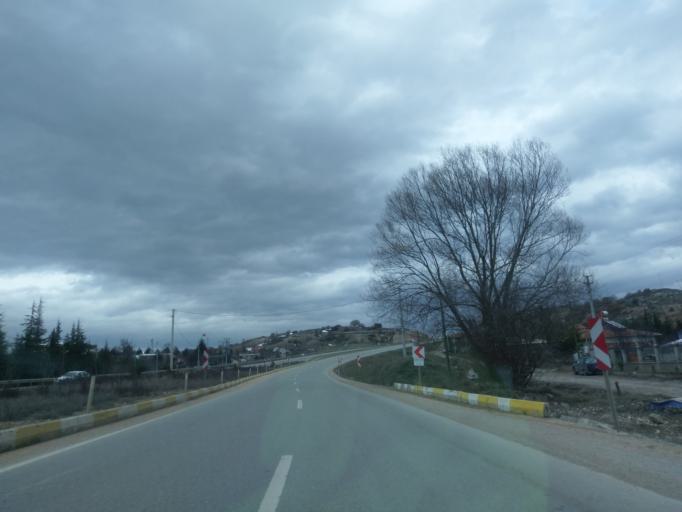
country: TR
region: Eskisehir
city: Eskisehir
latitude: 39.7341
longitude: 30.3835
